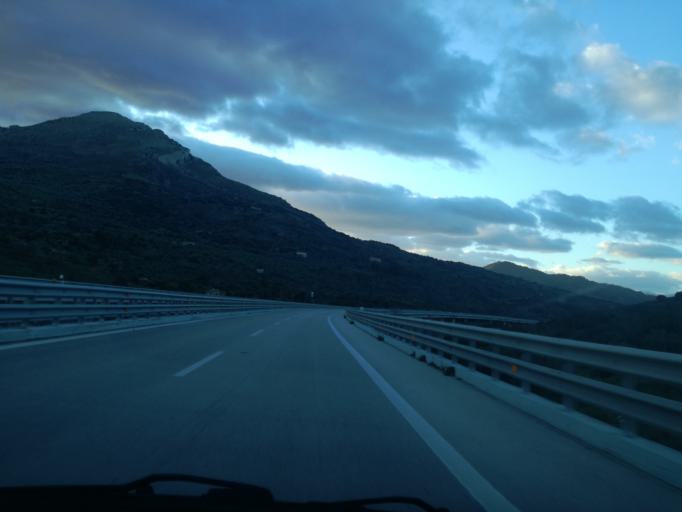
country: IT
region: Sicily
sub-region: Palermo
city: Scillato
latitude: 37.8359
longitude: 13.9314
